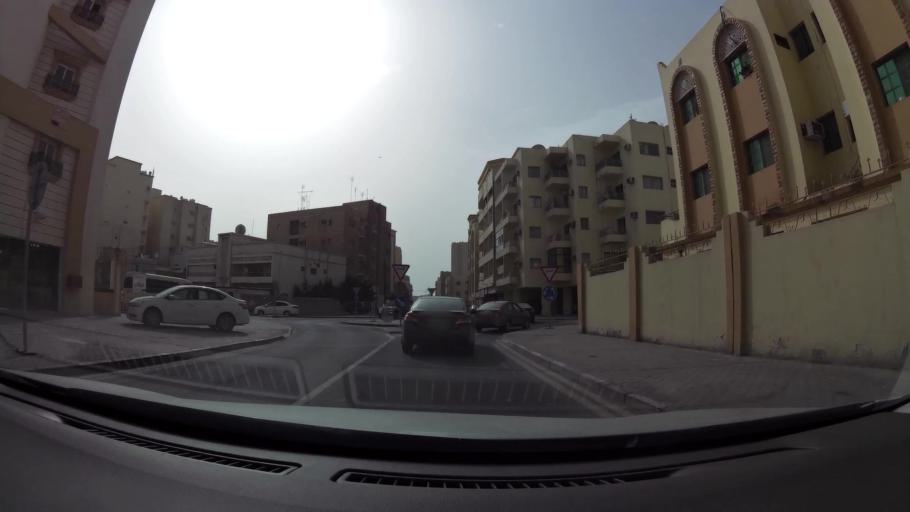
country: QA
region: Baladiyat ad Dawhah
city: Doha
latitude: 25.2772
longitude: 51.5434
